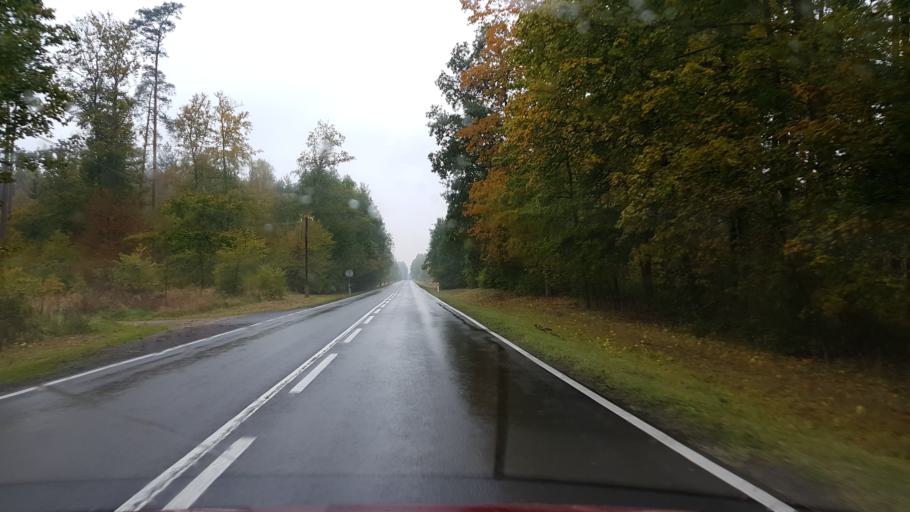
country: PL
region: Greater Poland Voivodeship
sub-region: Powiat zlotowski
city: Jastrowie
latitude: 53.3817
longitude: 16.7938
